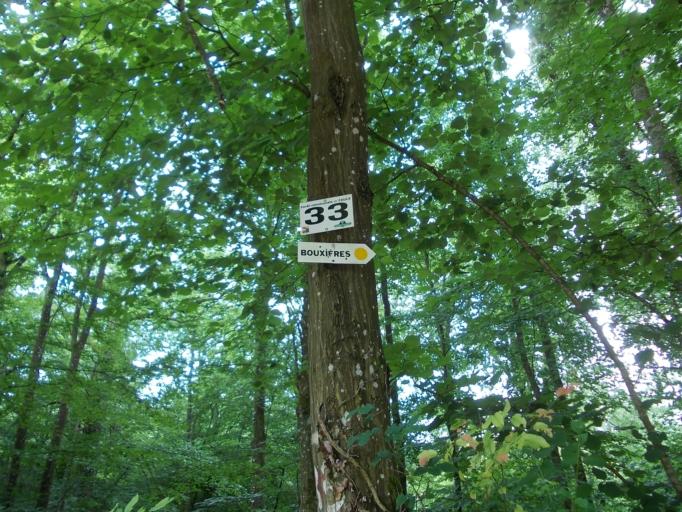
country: FR
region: Lorraine
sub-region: Departement de Meurthe-et-Moselle
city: Bouxieres-aux-Dames
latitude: 48.7749
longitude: 6.1734
